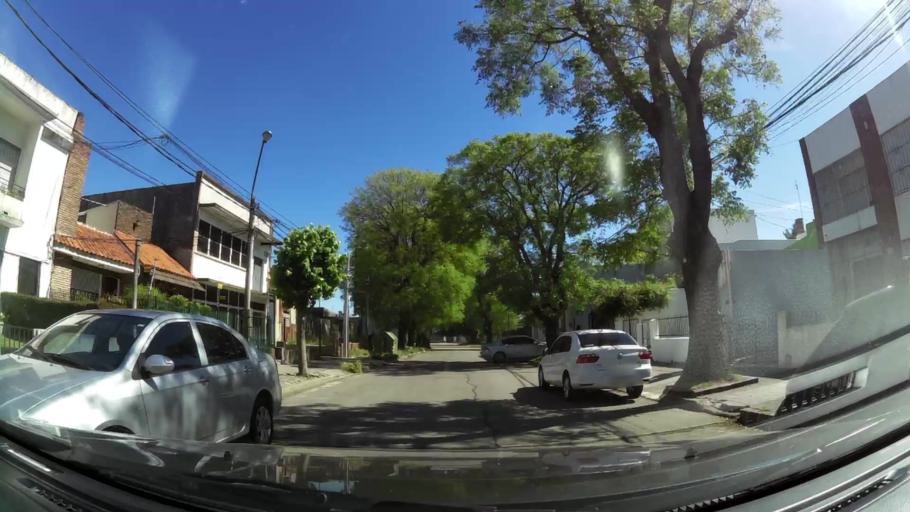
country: UY
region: Canelones
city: Paso de Carrasco
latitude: -34.8882
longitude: -56.1127
